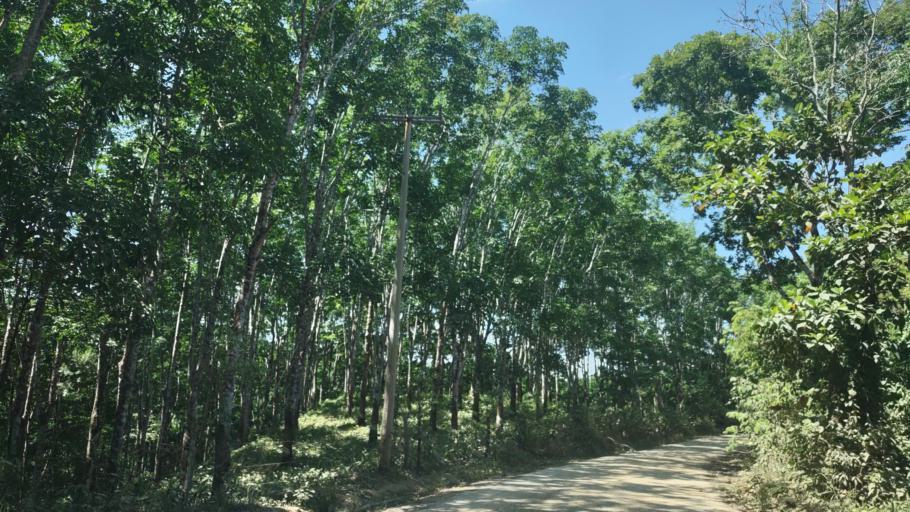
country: MX
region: Veracruz
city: Las Choapas
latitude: 17.7713
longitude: -94.1500
